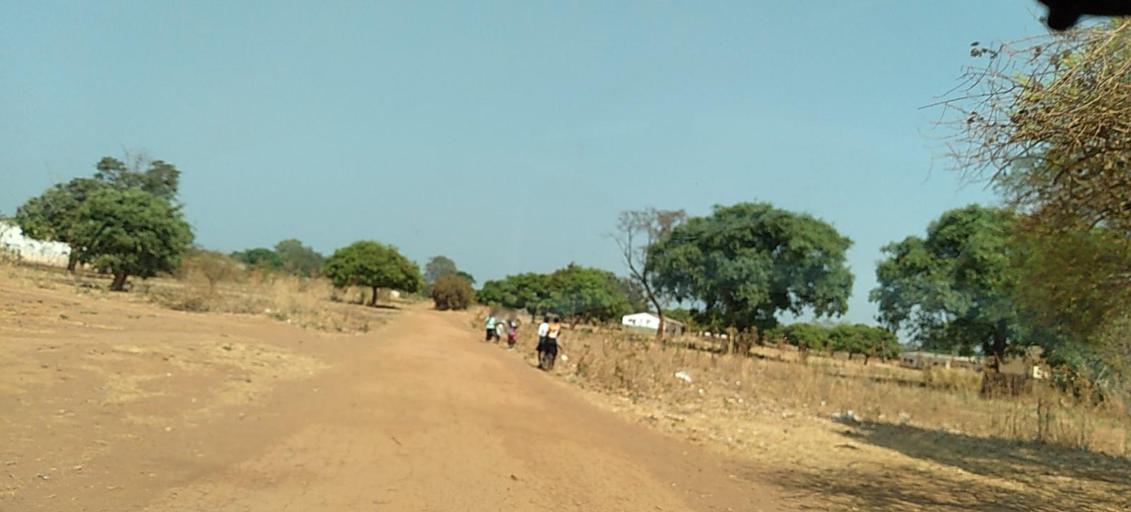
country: ZM
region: North-Western
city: Kasempa
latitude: -13.3896
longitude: 25.6747
